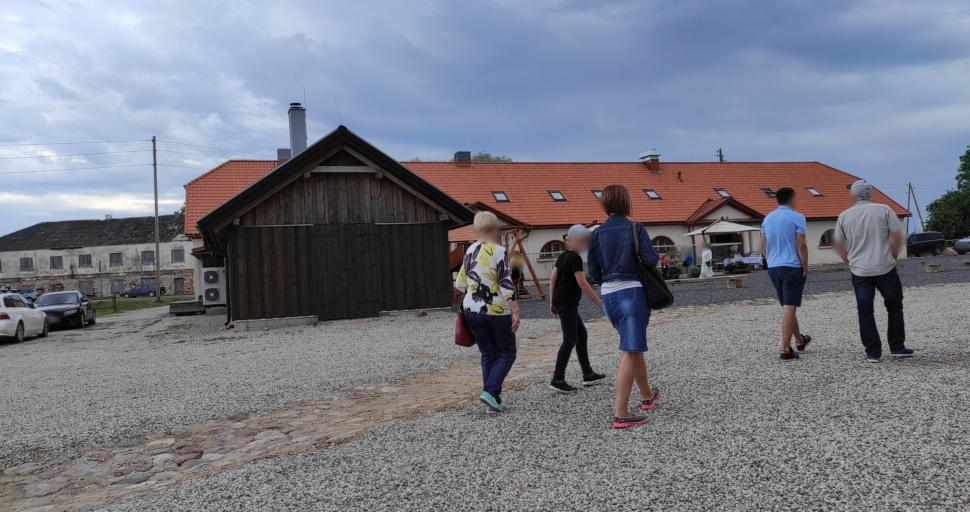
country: LV
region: Talsu Rajons
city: Talsi
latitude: 57.2256
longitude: 22.7641
